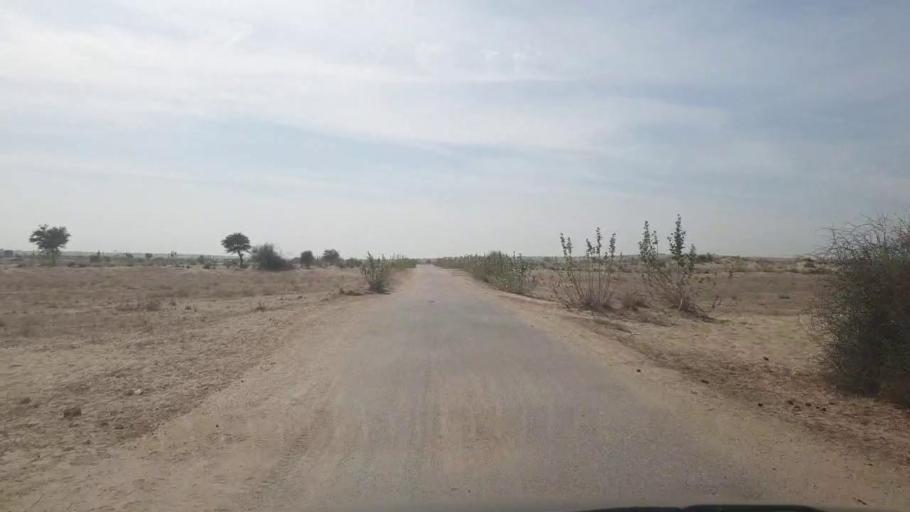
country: PK
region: Sindh
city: Umarkot
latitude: 25.2891
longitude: 69.7283
